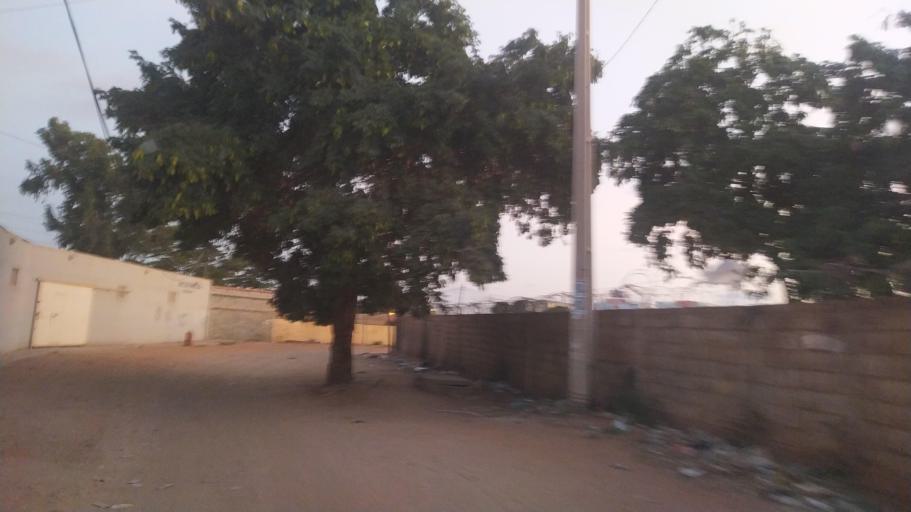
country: AO
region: Luanda
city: Luanda
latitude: -8.8992
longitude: 13.2042
